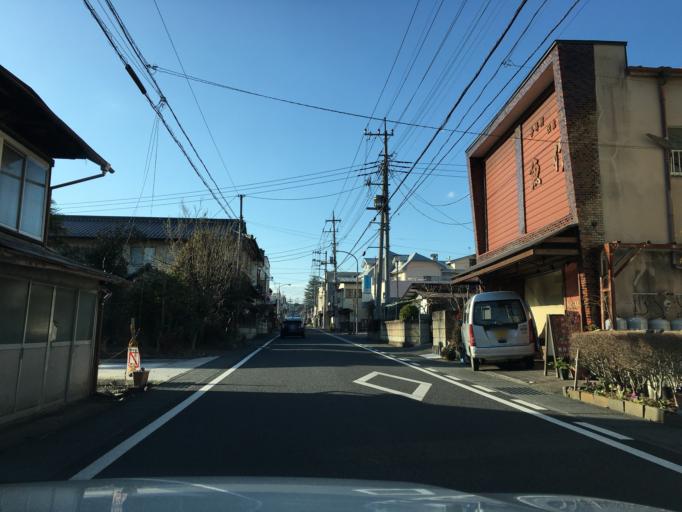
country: JP
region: Ibaraki
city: Daigo
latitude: 36.7741
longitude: 140.3496
